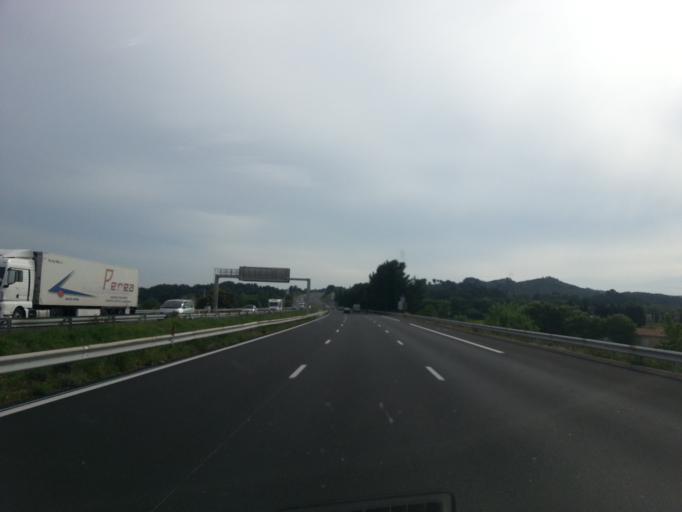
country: FR
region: Languedoc-Roussillon
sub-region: Departement du Gard
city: Tavel
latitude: 44.0111
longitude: 4.7145
